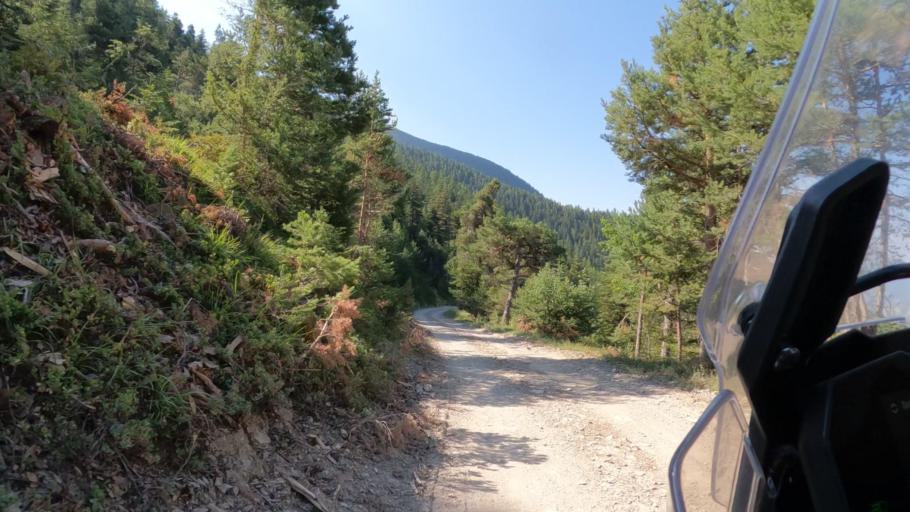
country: FR
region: Provence-Alpes-Cote d'Azur
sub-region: Departement des Hautes-Alpes
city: Embrun
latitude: 44.5922
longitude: 6.5618
